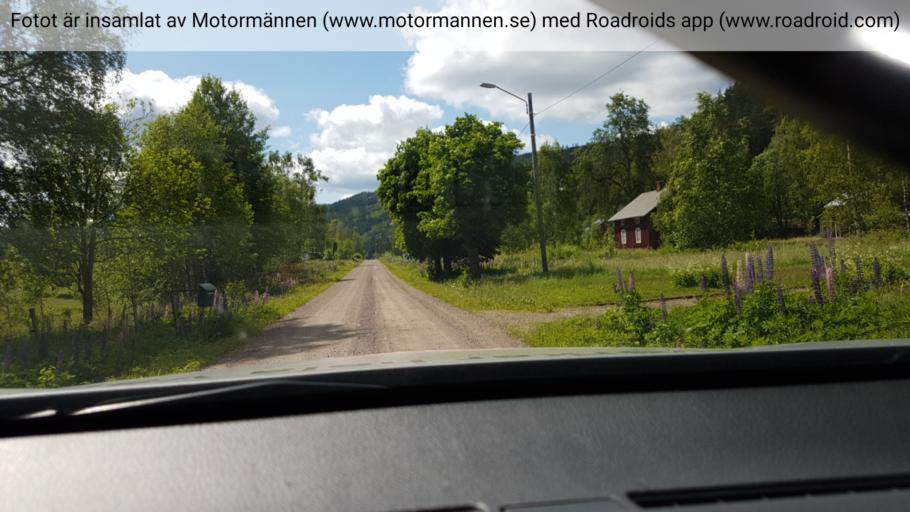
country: SE
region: Vaermland
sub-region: Hagfors Kommun
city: Ekshaerad
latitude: 60.3221
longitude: 13.3720
